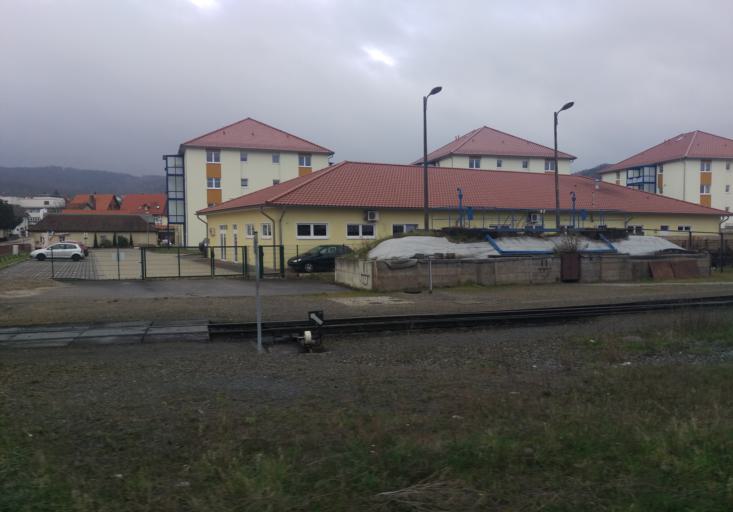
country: DE
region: Saxony-Anhalt
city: Wernigerode
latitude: 51.8386
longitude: 10.7735
